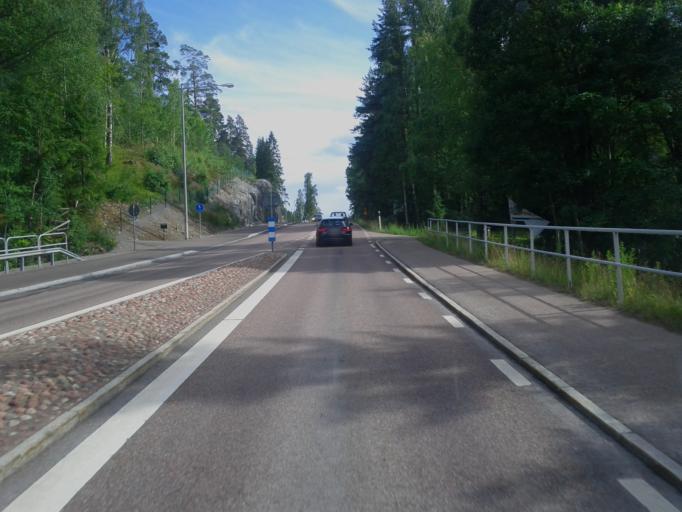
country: SE
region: Dalarna
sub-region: Faluns Kommun
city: Grycksbo
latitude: 60.6798
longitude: 15.5070
